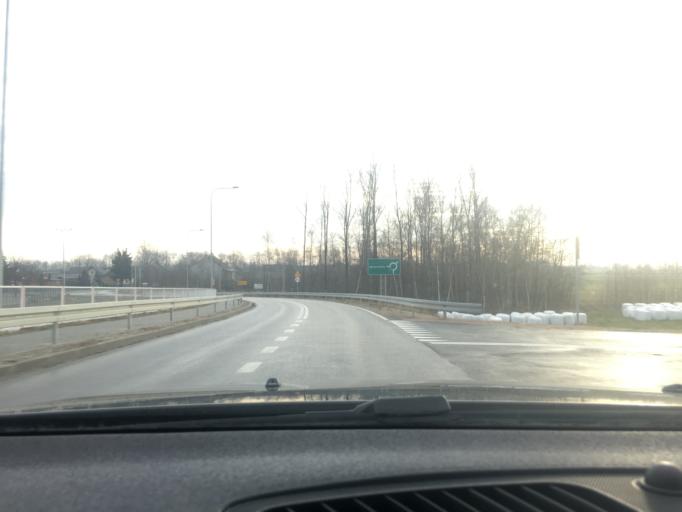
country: PL
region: Swietokrzyskie
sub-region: Powiat jedrzejowski
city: Jedrzejow
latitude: 50.6589
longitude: 20.3326
